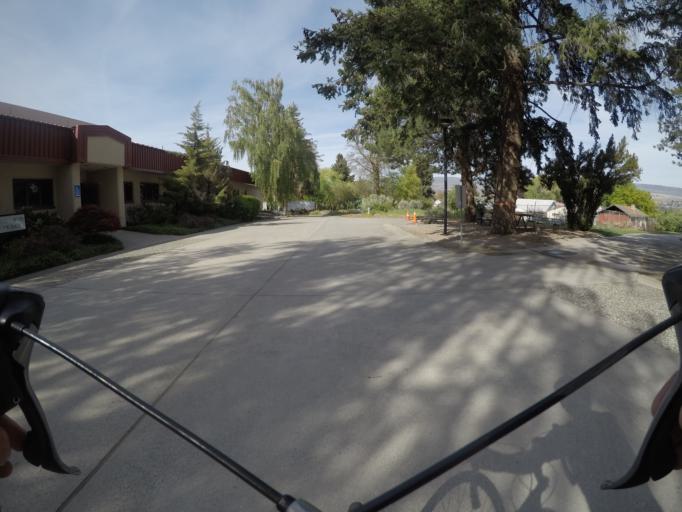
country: US
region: Washington
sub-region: Chelan County
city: West Wenatchee
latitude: 47.4318
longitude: -120.3354
